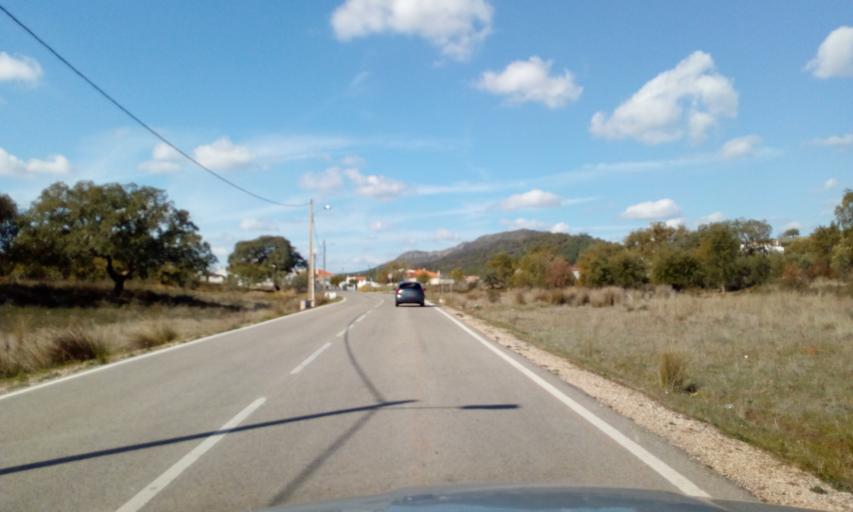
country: PT
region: Faro
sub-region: Loule
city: Loule
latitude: 37.2442
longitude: -8.0618
